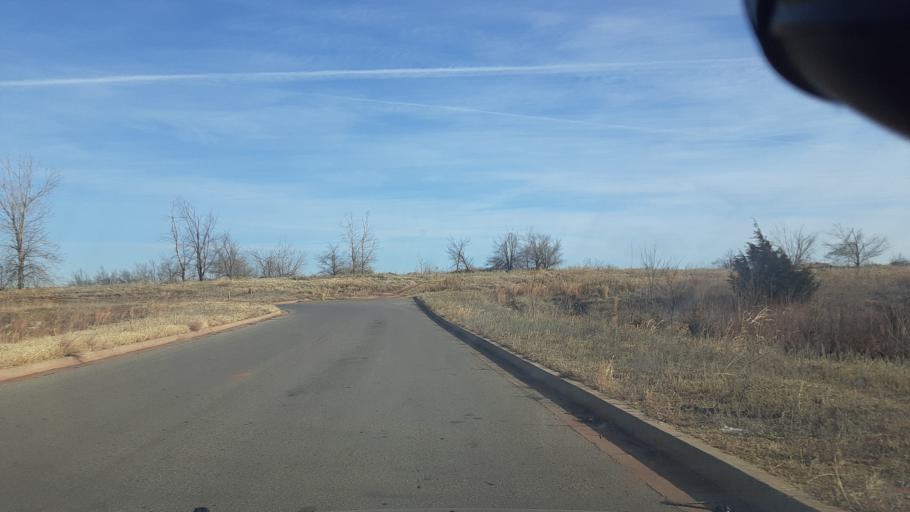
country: US
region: Oklahoma
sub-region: Logan County
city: Guthrie
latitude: 35.8593
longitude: -97.4232
